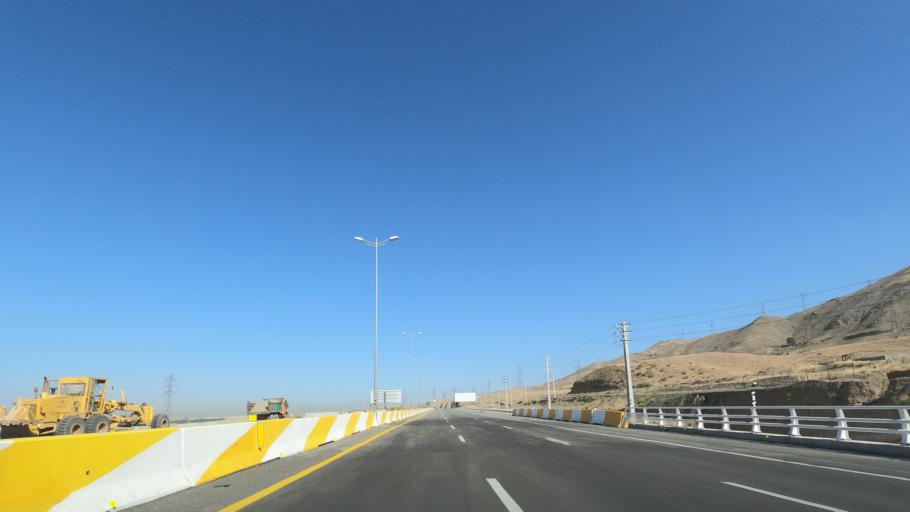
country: IR
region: Tehran
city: Shahr-e Qods
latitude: 35.7682
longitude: 51.0641
